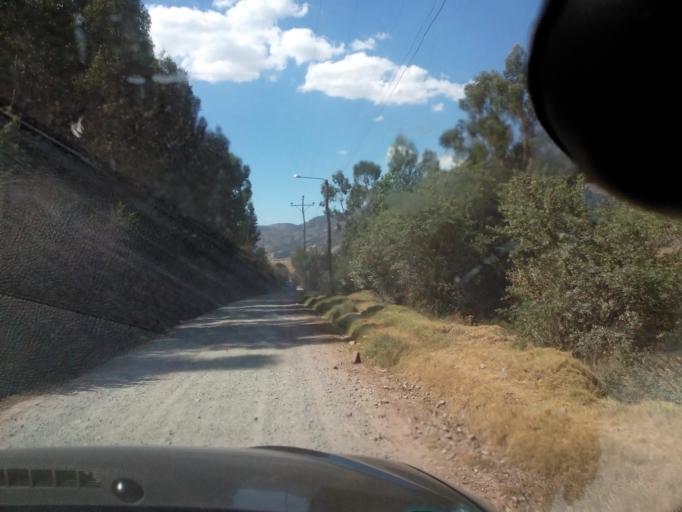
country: PE
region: Cusco
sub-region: Provincia de Anta
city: Huarocondo
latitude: -13.4331
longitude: -72.2235
